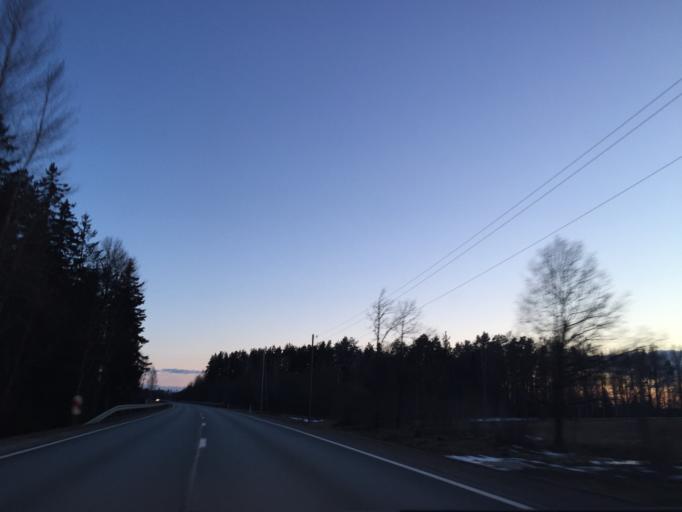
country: LV
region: Krimulda
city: Ragana
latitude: 57.2174
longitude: 24.7871
